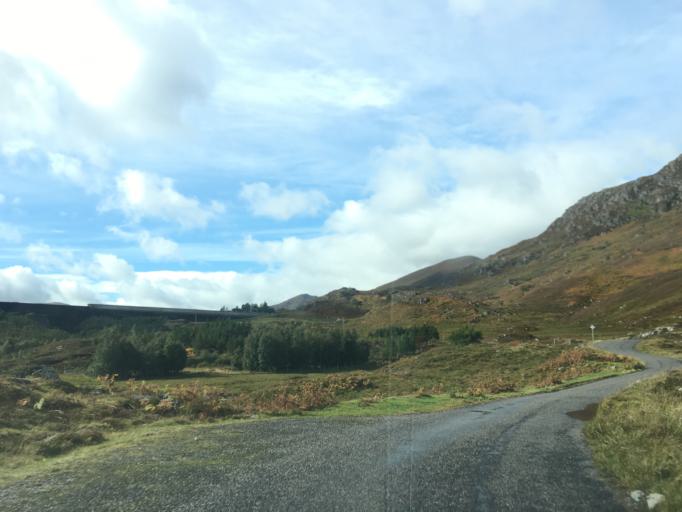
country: GB
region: Scotland
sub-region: Highland
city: Spean Bridge
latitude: 57.3405
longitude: -4.9478
